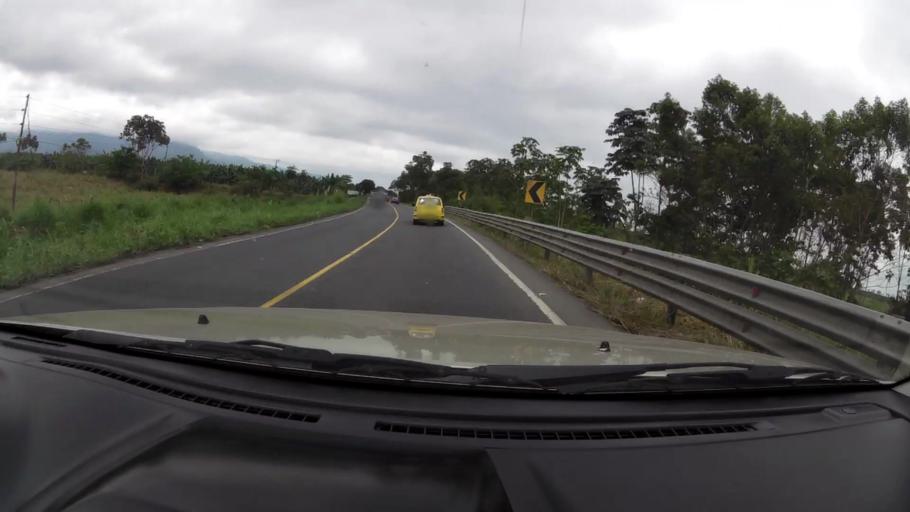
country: EC
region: Guayas
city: Naranjal
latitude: -2.7142
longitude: -79.6706
